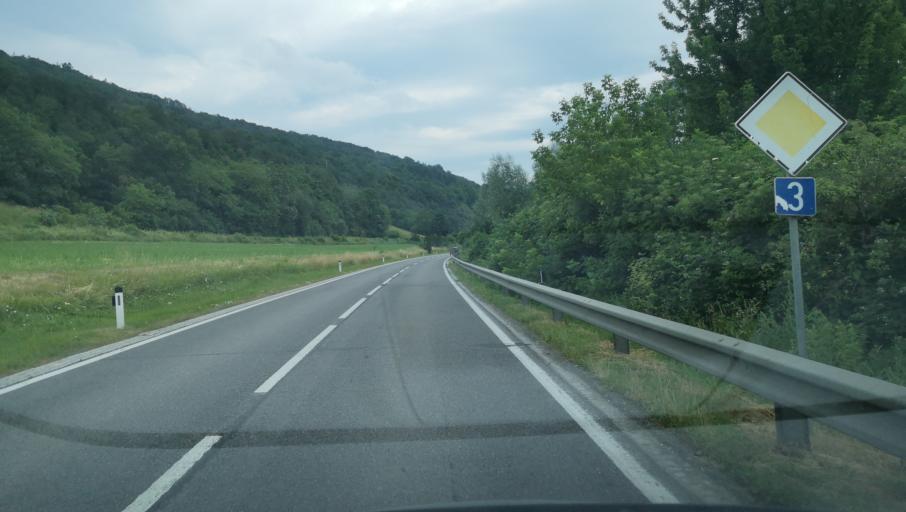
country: AT
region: Lower Austria
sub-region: Politischer Bezirk Melk
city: Klein-Poechlarn
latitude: 48.2205
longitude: 15.2353
